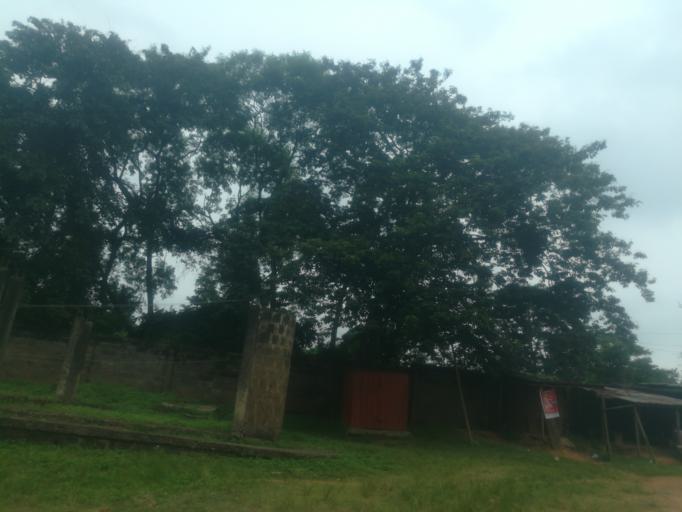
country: NG
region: Oyo
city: Ibadan
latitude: 7.3872
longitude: 3.9337
